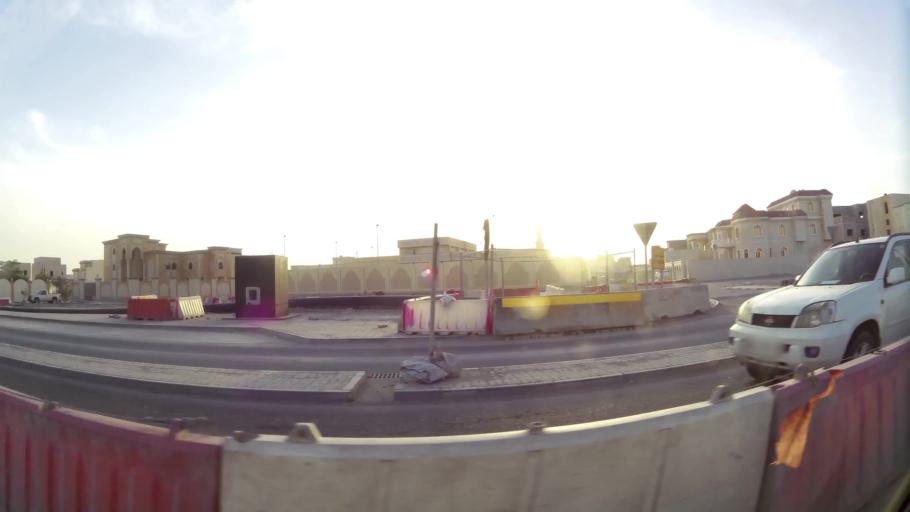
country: QA
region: Al Wakrah
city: Al Wakrah
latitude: 25.1603
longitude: 51.5910
